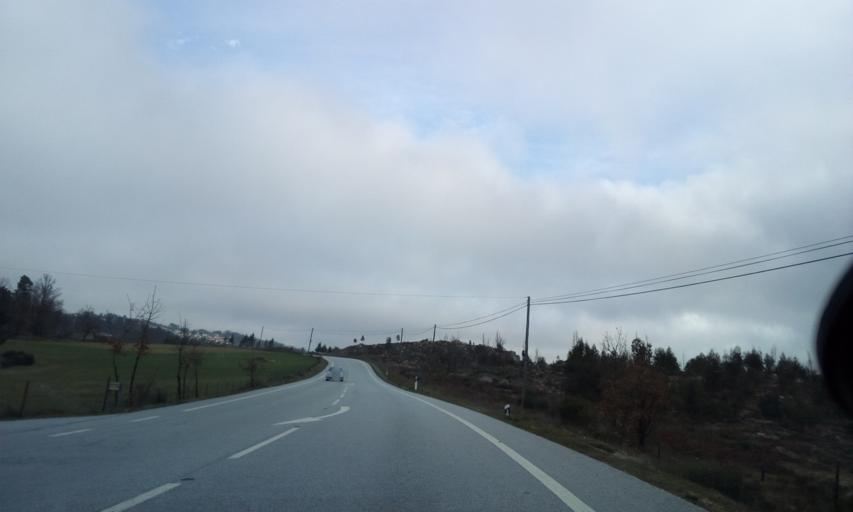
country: PT
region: Guarda
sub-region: Fornos de Algodres
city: Fornos de Algodres
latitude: 40.6701
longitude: -7.4745
